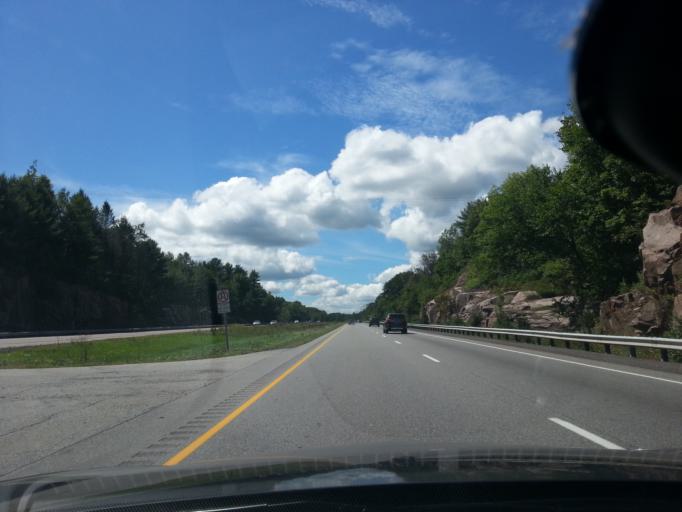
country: CA
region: Ontario
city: Brockville
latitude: 44.5189
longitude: -75.8133
